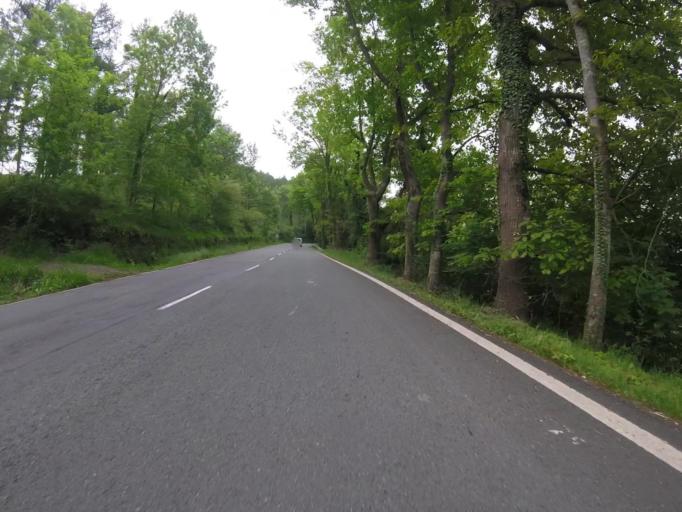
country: ES
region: Navarre
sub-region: Provincia de Navarra
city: Zugarramurdi
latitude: 43.2629
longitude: -1.4895
